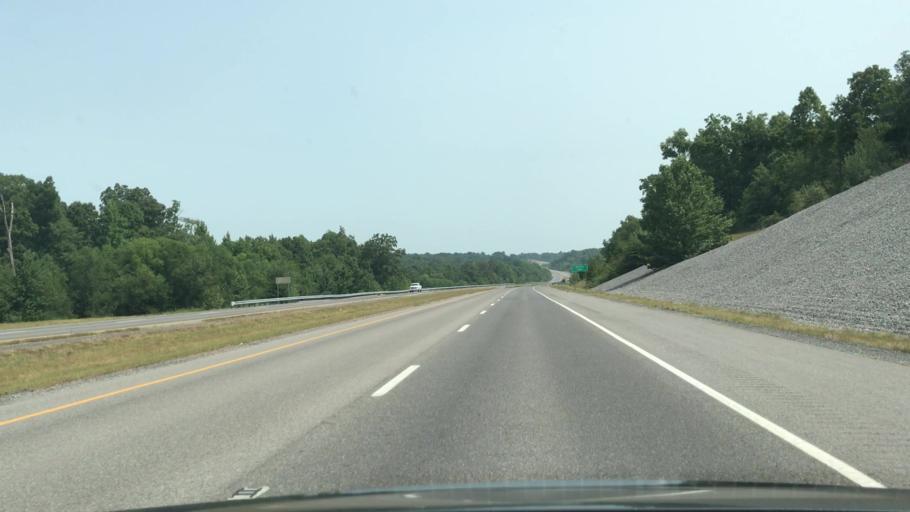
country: US
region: Kentucky
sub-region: Calloway County
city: Murray
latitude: 36.7479
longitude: -88.1594
